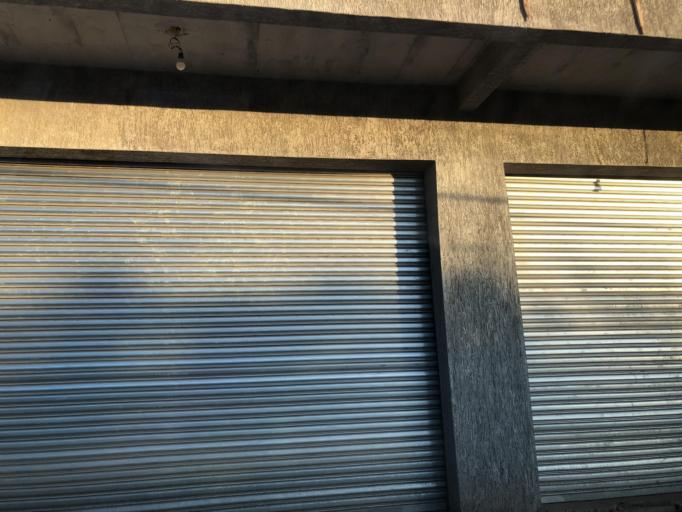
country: BR
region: Federal District
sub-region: Brasilia
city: Brasilia
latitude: -15.8833
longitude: -47.7690
